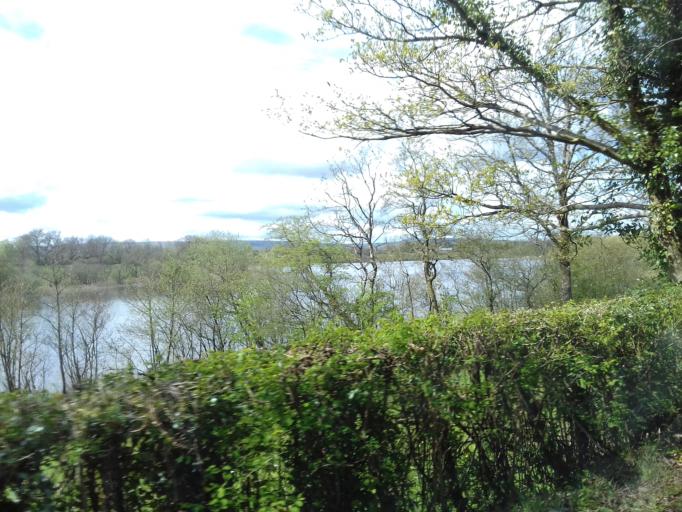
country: GB
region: Northern Ireland
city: Lisnaskea
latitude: 54.1870
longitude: -7.4894
